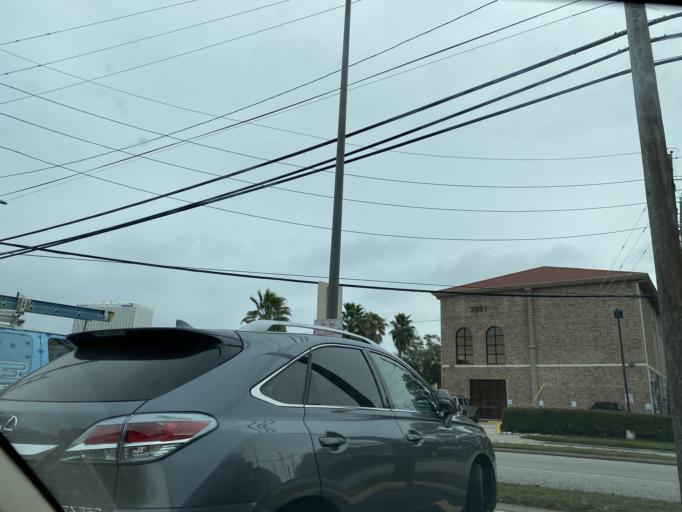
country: US
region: Texas
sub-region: Harris County
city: Bellaire
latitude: 29.7347
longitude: -95.4767
